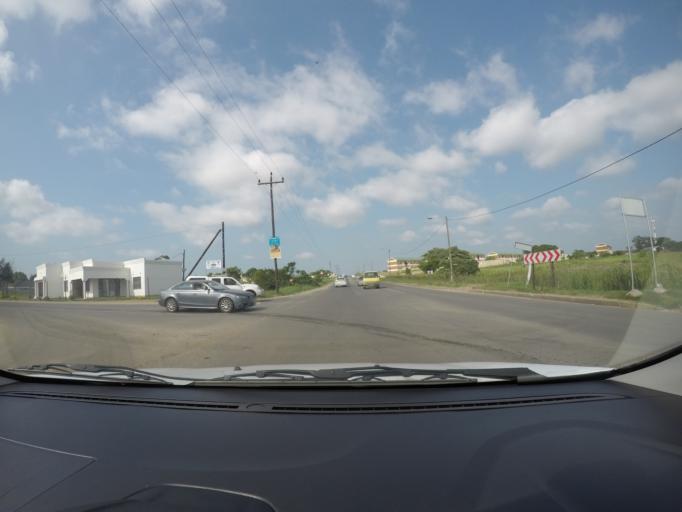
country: ZA
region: KwaZulu-Natal
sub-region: uThungulu District Municipality
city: eSikhawini
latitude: -28.8816
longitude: 31.9061
